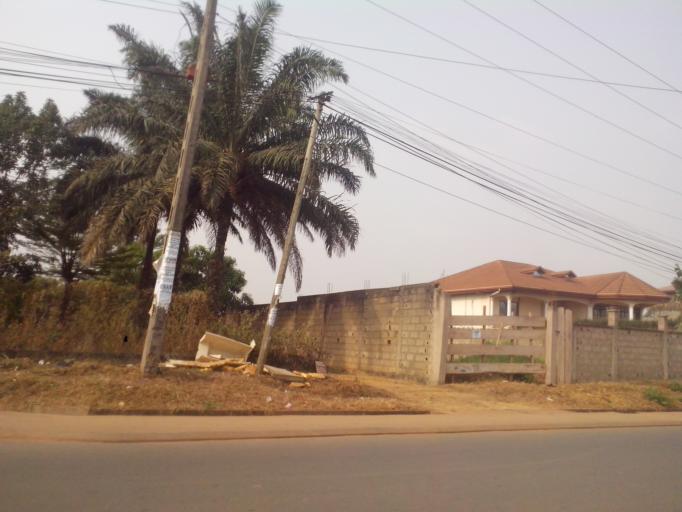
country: CM
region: Centre
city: Yaounde
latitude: 3.8458
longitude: 11.4983
